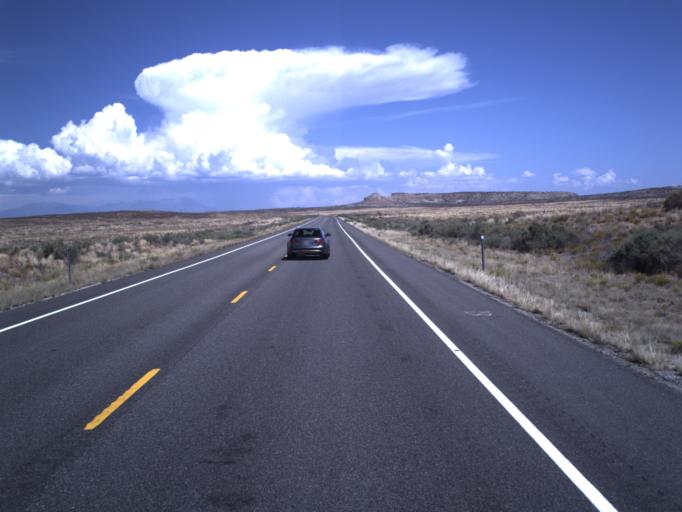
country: US
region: Utah
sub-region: San Juan County
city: Blanding
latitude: 37.3211
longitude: -109.5233
